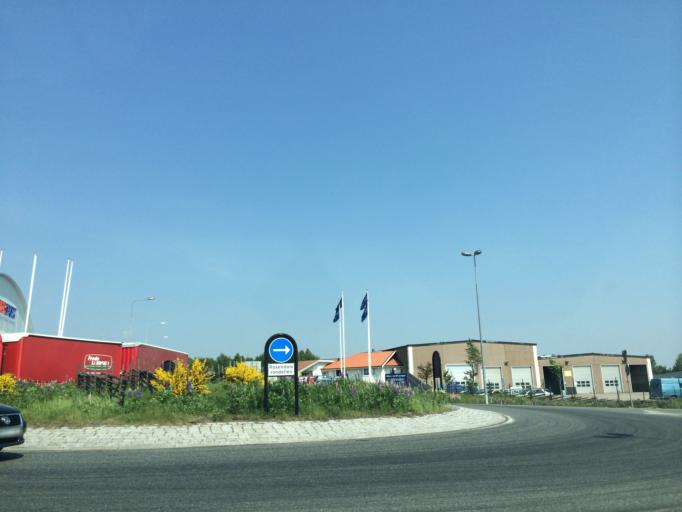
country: SE
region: Kronoberg
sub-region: Ljungby Kommun
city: Ljungby
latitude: 56.8130
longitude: 13.9092
